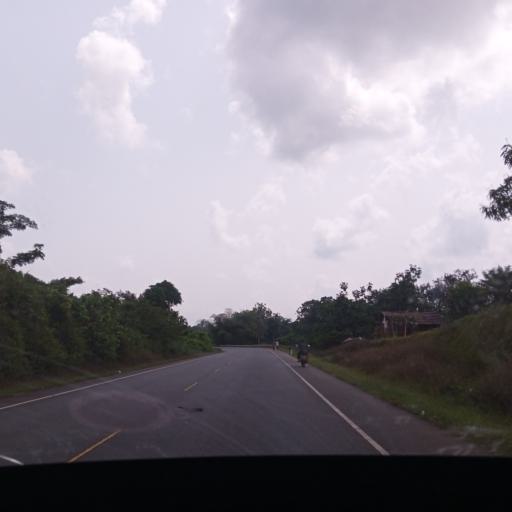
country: LR
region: Margibi
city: Kakata
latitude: 6.2456
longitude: -10.2921
